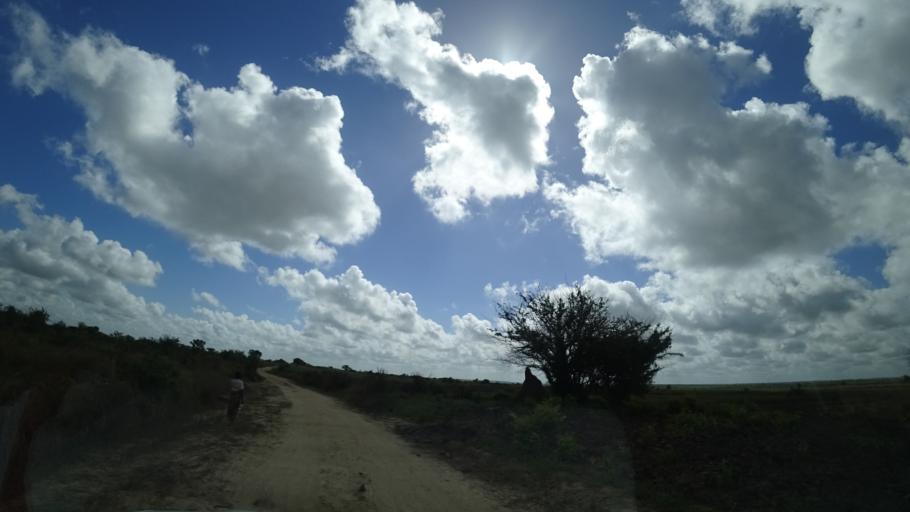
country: MZ
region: Sofala
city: Dondo
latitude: -19.4173
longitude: 34.5655
